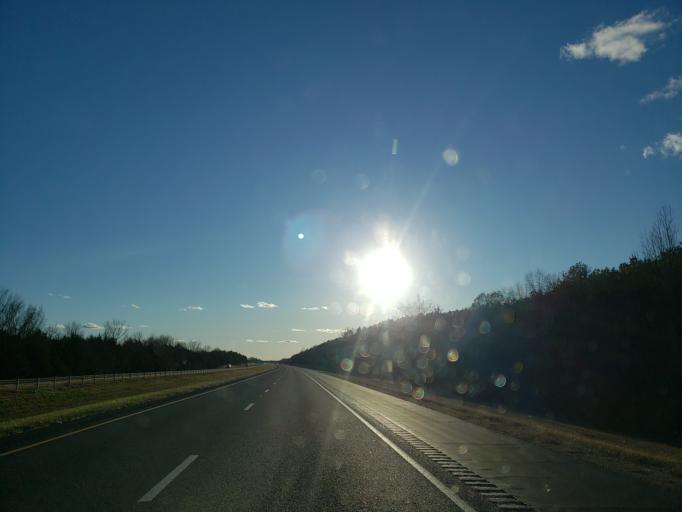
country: US
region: Alabama
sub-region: Sumter County
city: Livingston
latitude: 32.7112
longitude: -88.1320
